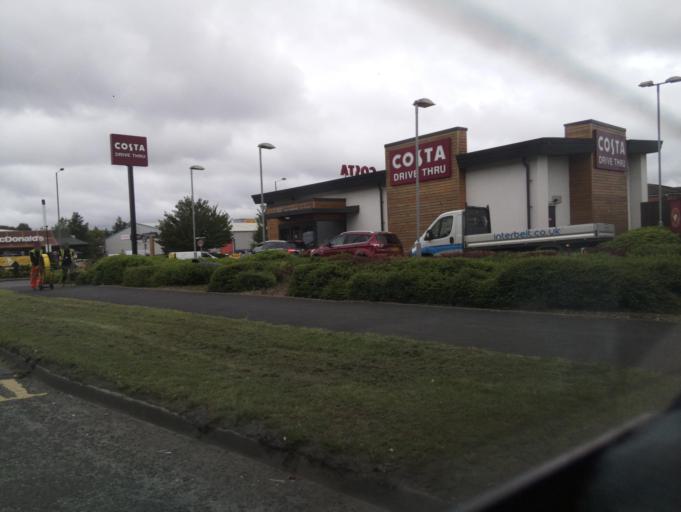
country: GB
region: England
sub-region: Staffordshire
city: Burton upon Trent
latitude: 52.8269
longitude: -1.6186
